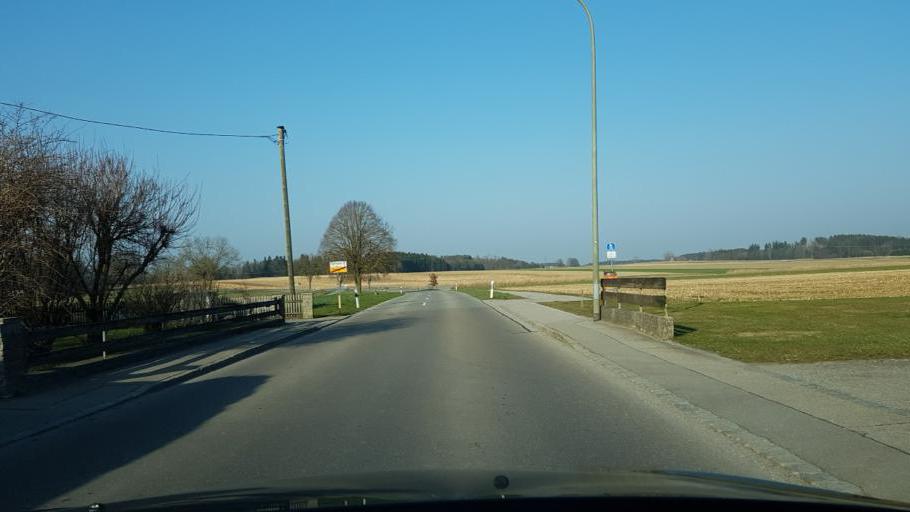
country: DE
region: Bavaria
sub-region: Upper Bavaria
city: Egenhofen
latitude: 48.2727
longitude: 11.1661
